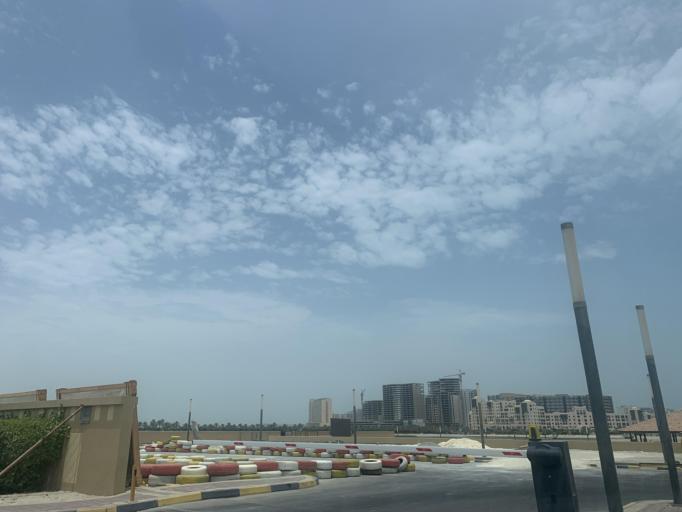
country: BH
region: Muharraq
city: Al Hadd
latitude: 26.2782
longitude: 50.6686
